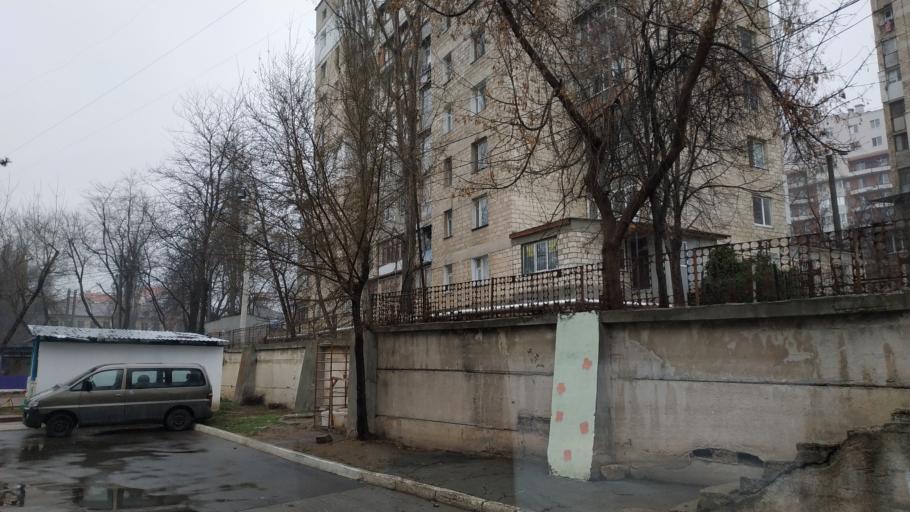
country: MD
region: Chisinau
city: Chisinau
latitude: 47.0201
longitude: 28.7999
